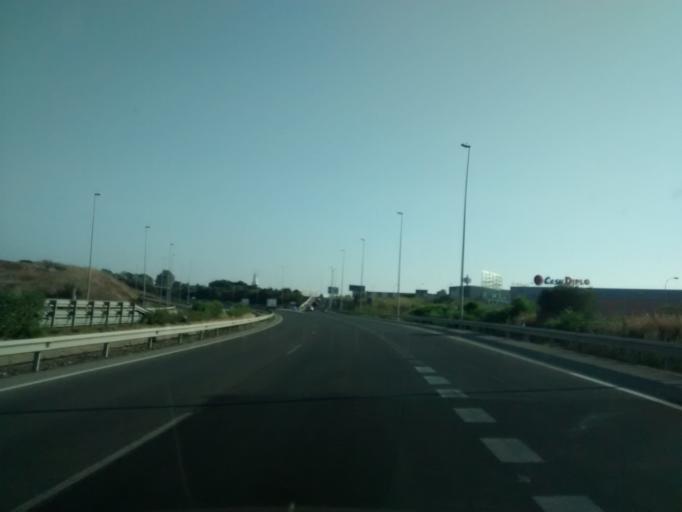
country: ES
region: Andalusia
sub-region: Provincia de Cadiz
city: Chiclana de la Frontera
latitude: 36.4029
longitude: -6.1263
